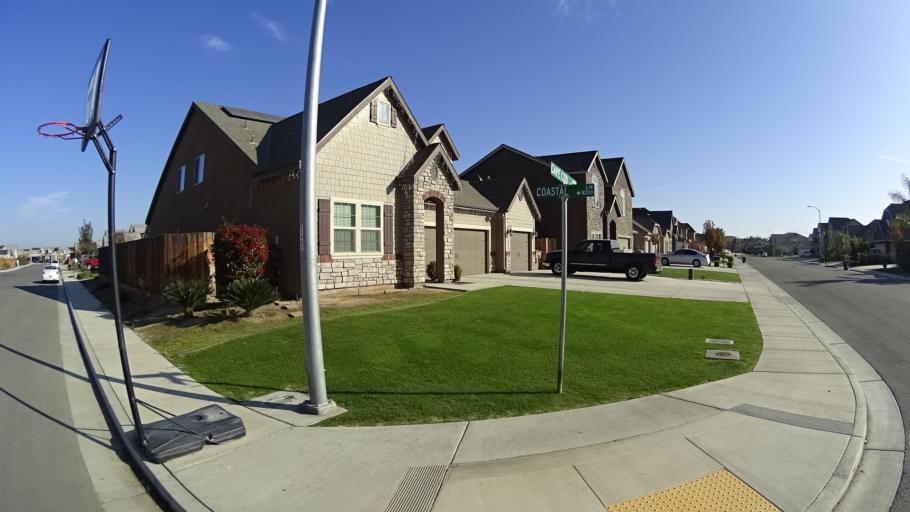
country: US
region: California
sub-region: Kern County
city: Greenfield
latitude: 35.2705
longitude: -119.0707
